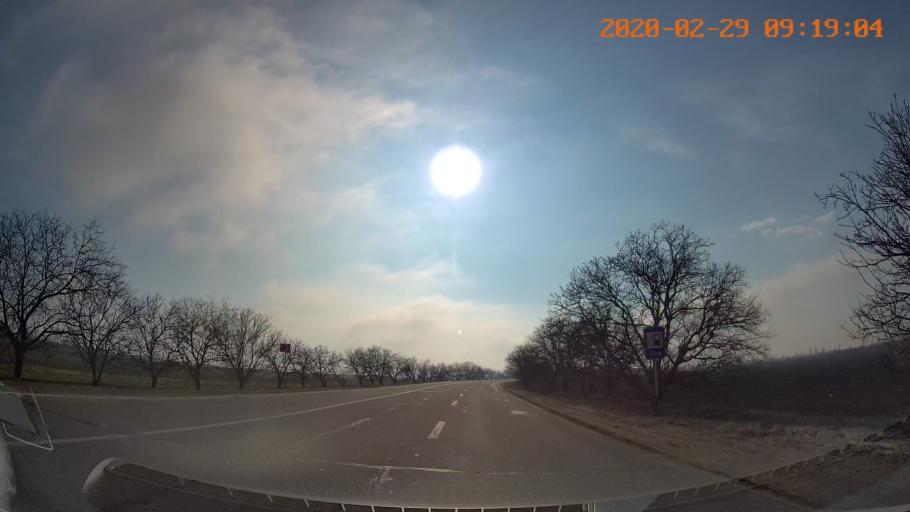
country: MD
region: Telenesti
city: Pervomaisc
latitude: 46.7675
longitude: 29.9347
